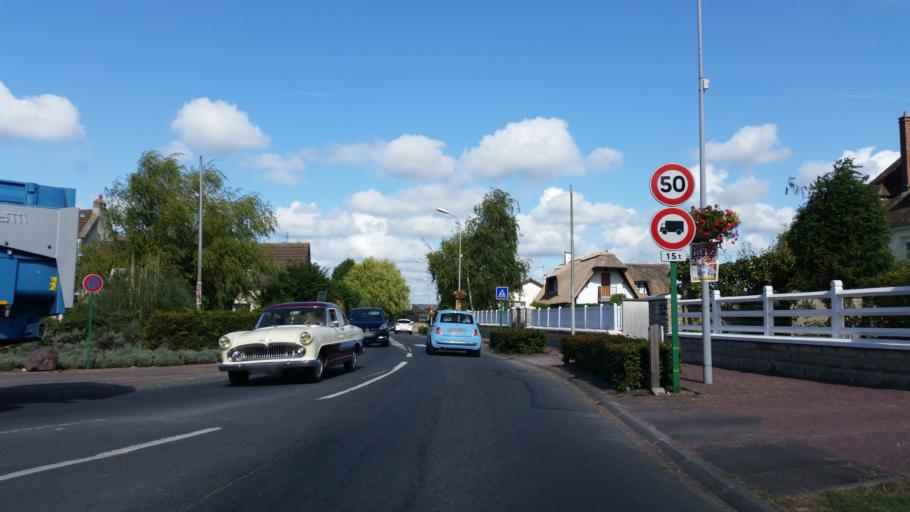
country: FR
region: Lower Normandy
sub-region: Departement du Calvados
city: Bavent
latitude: 49.2533
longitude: -0.1609
